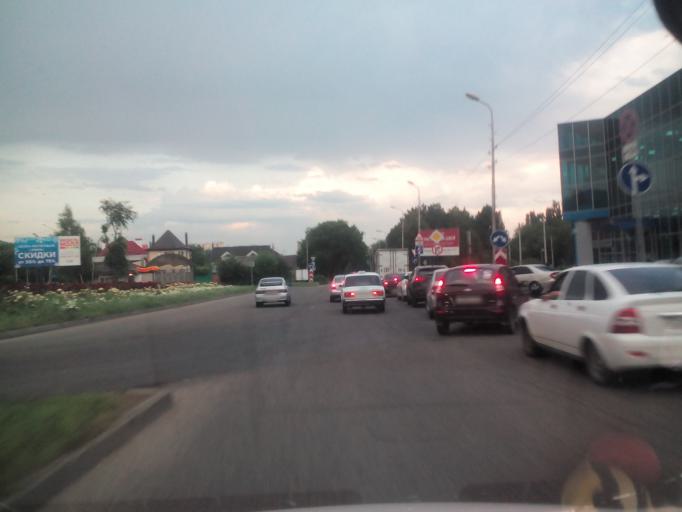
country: RU
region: Stavropol'skiy
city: Svobody
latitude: 44.0404
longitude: 43.0340
